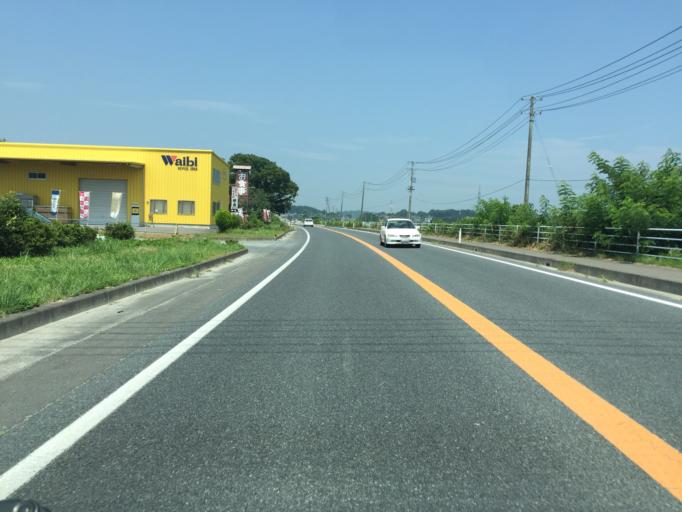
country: JP
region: Miyagi
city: Marumori
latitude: 37.8249
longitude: 140.9196
